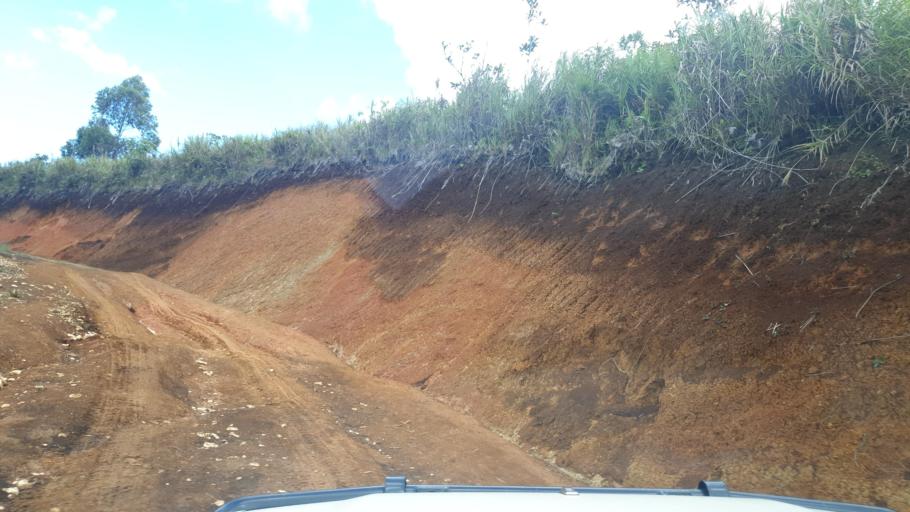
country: PG
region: Eastern Highlands
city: Goroka
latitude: -6.2794
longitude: 145.1909
